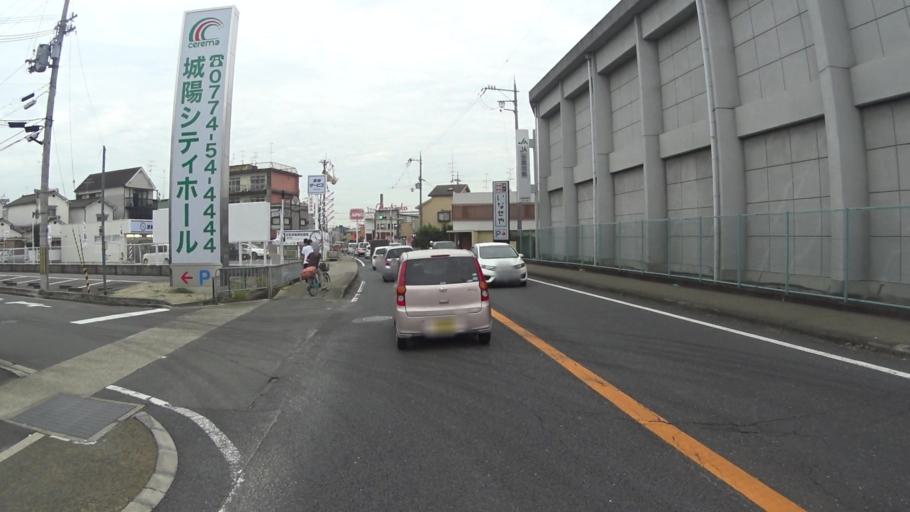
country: JP
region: Kyoto
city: Tanabe
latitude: 34.8576
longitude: 135.7767
